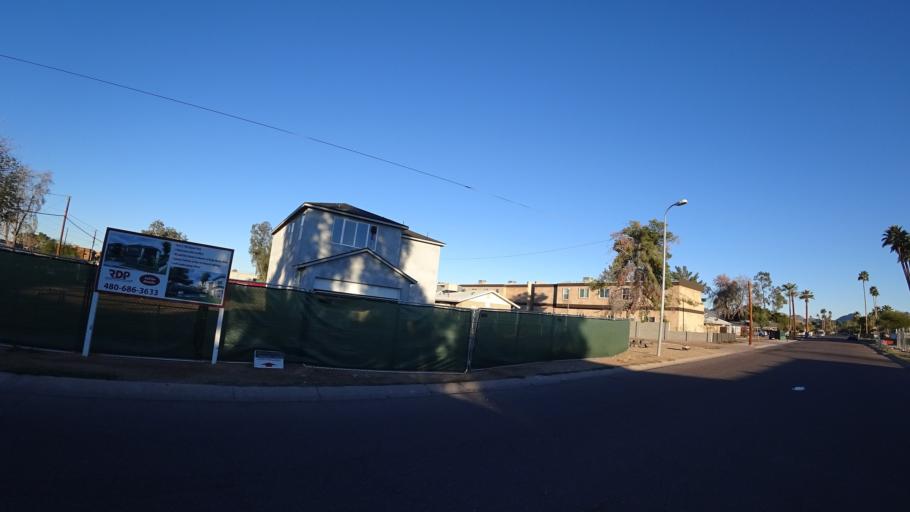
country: US
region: Arizona
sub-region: Maricopa County
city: Paradise Valley
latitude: 33.4843
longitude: -112.0020
